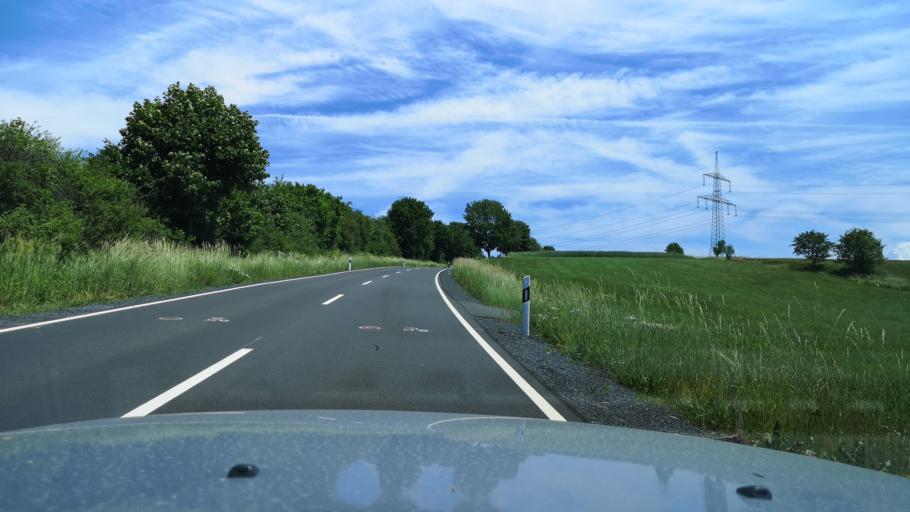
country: DE
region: Bavaria
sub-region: Upper Franconia
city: Tschirn
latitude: 50.3977
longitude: 11.4528
